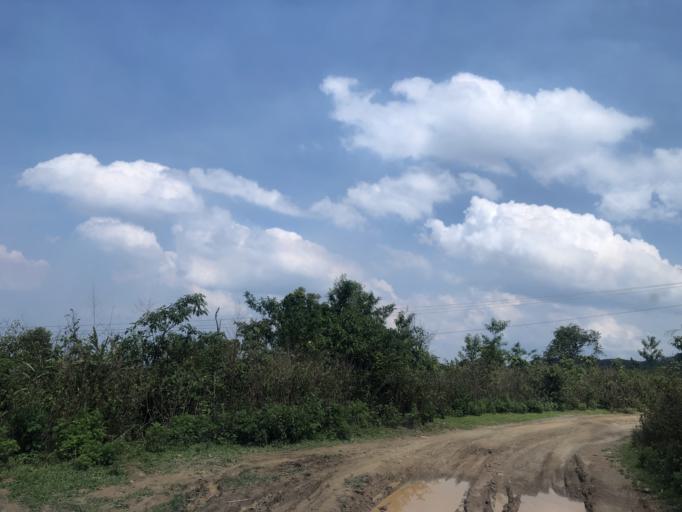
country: LA
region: Phongsali
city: Phongsali
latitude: 21.3942
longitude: 102.1919
